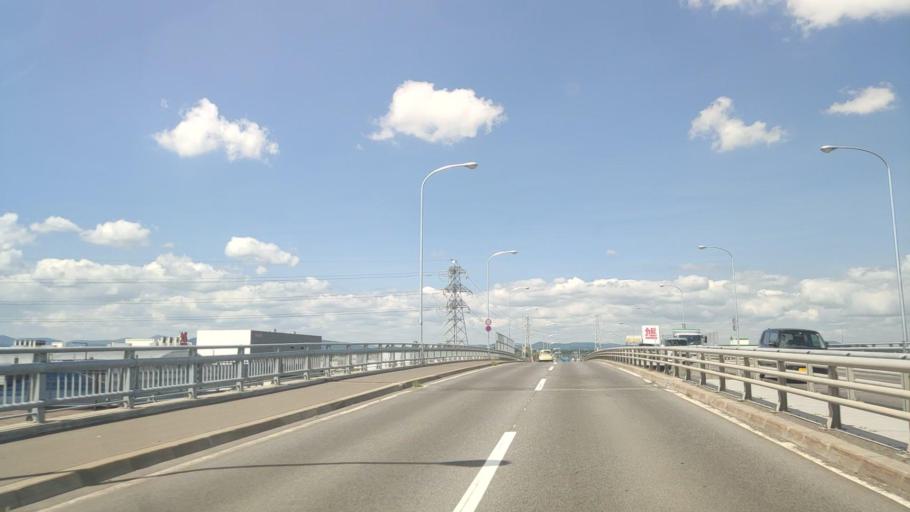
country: JP
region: Hokkaido
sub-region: Asahikawa-shi
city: Asahikawa
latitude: 43.7933
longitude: 142.4016
